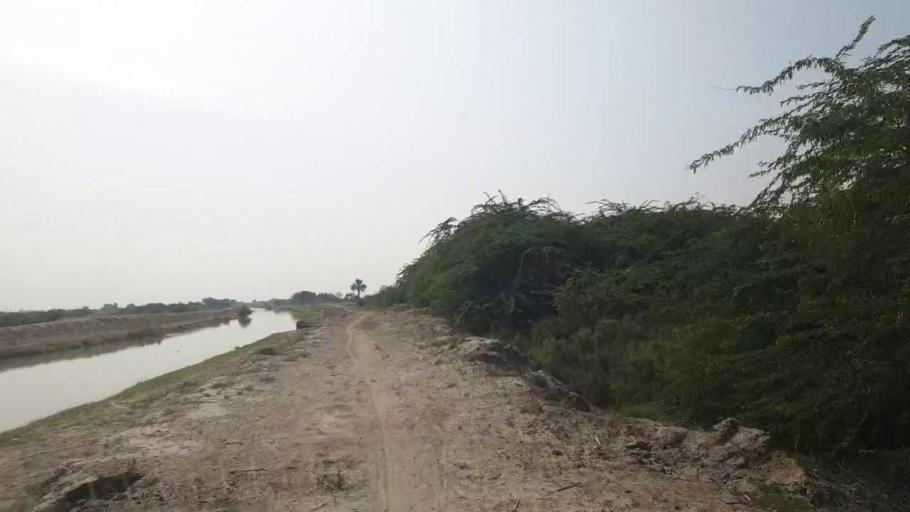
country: PK
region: Sindh
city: Badin
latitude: 24.5634
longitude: 68.8501
